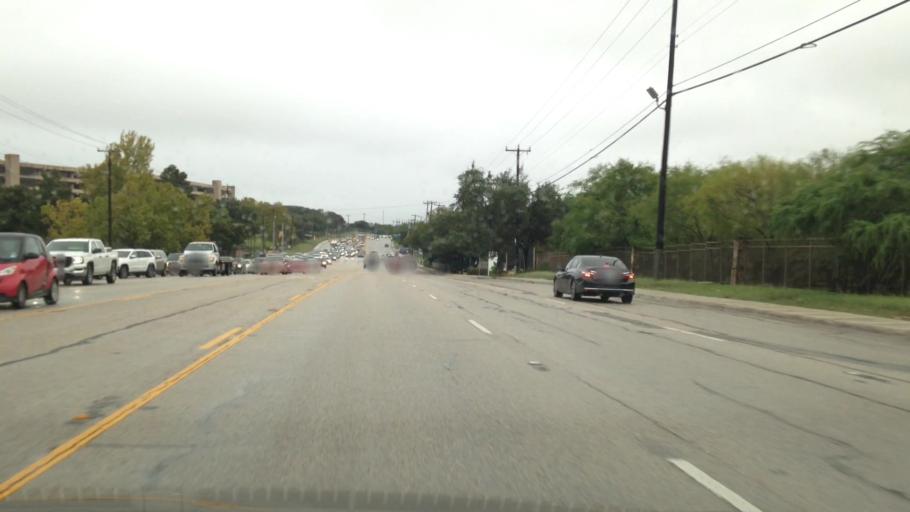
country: US
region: Texas
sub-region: Bexar County
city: Shavano Park
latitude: 29.5395
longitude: -98.5795
